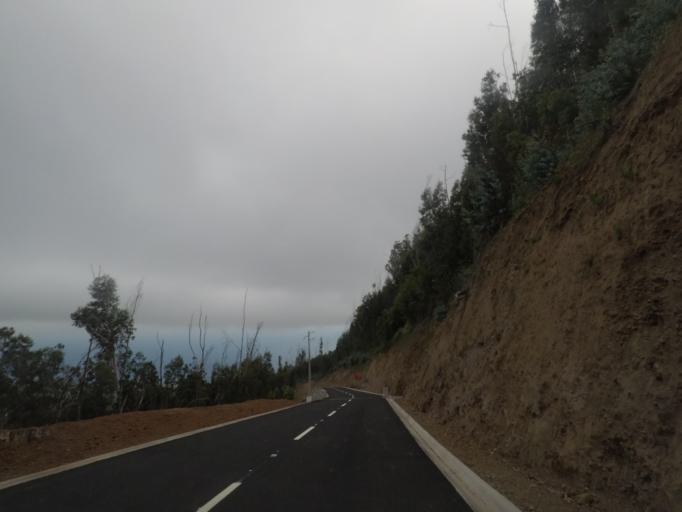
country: PT
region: Madeira
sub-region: Calheta
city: Arco da Calheta
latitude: 32.7528
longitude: -17.1515
